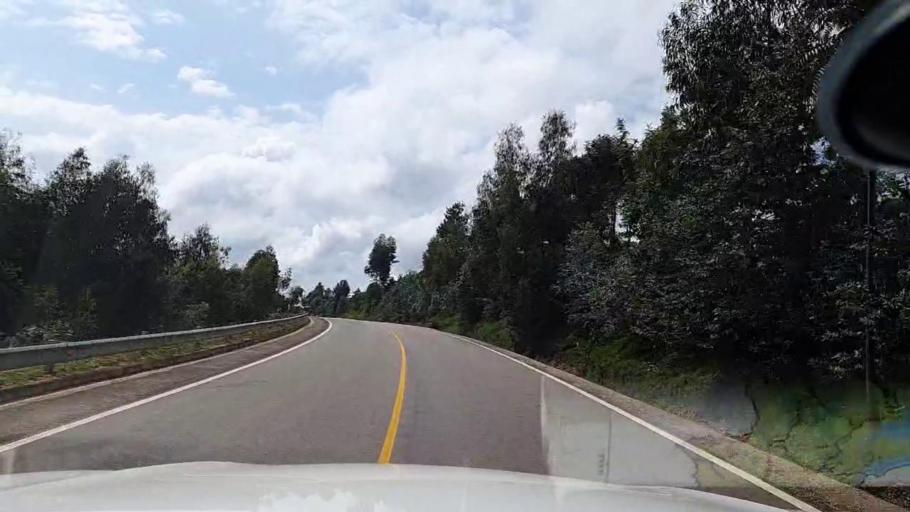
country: RW
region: Southern Province
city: Nzega
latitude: -2.4971
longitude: 29.5066
